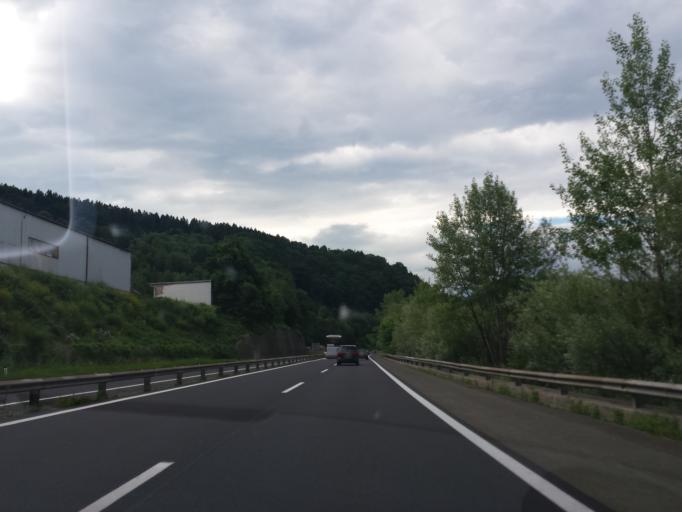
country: AT
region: Styria
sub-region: Politischer Bezirk Bruck-Muerzzuschlag
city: Bruck an der Mur
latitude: 47.3967
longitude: 15.2852
